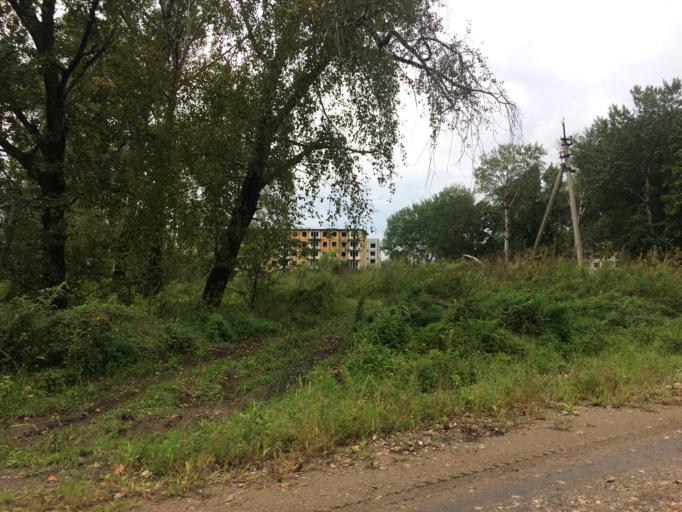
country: RU
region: Primorskiy
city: Lazo
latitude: 45.8223
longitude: 133.6441
